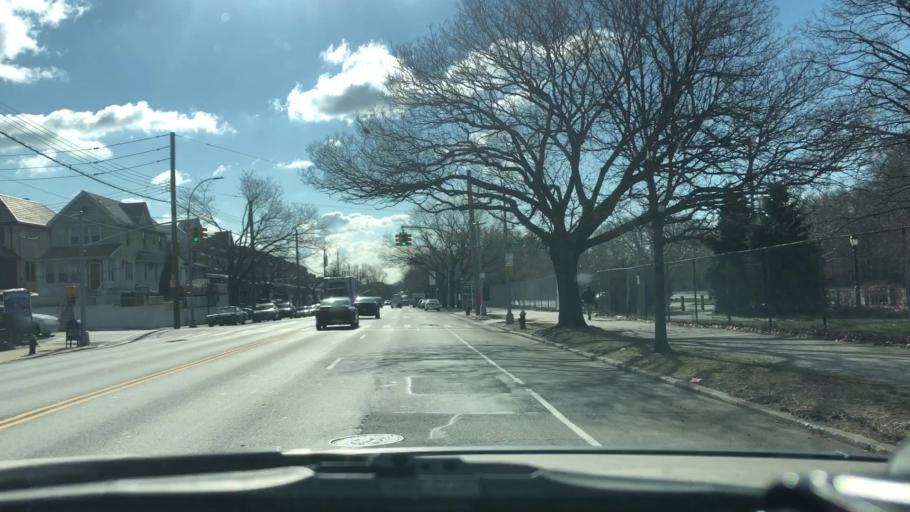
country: US
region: New York
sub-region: Kings County
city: Bensonhurst
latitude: 40.6170
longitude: -74.0188
